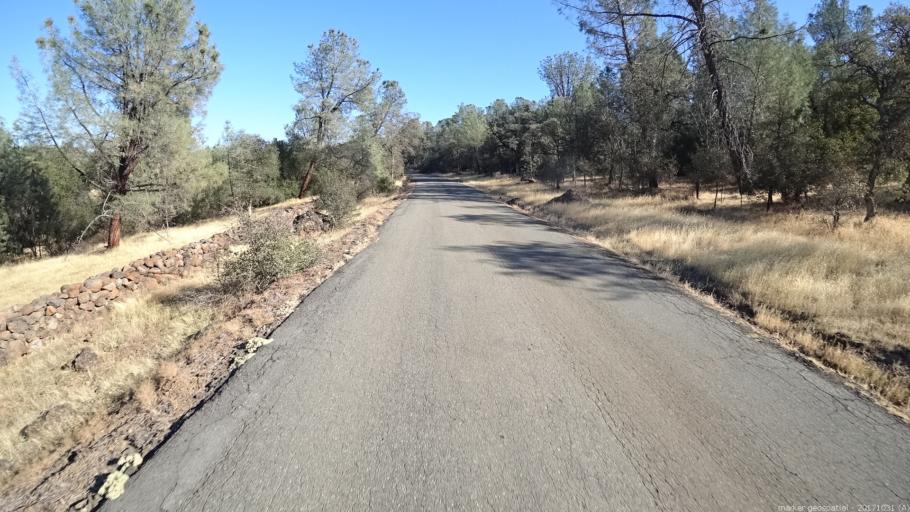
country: US
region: California
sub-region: Shasta County
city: Shingletown
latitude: 40.4593
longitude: -122.0595
